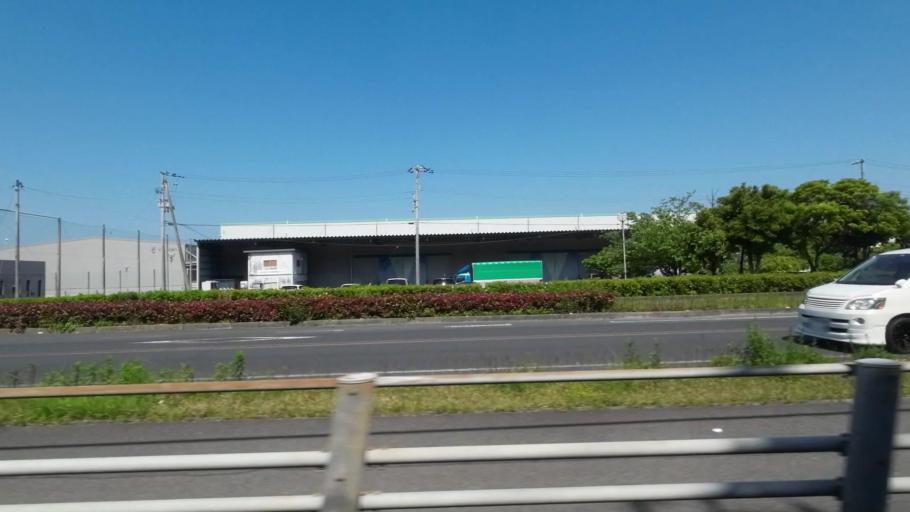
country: JP
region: Ehime
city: Kawanoecho
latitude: 34.0252
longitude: 133.5812
